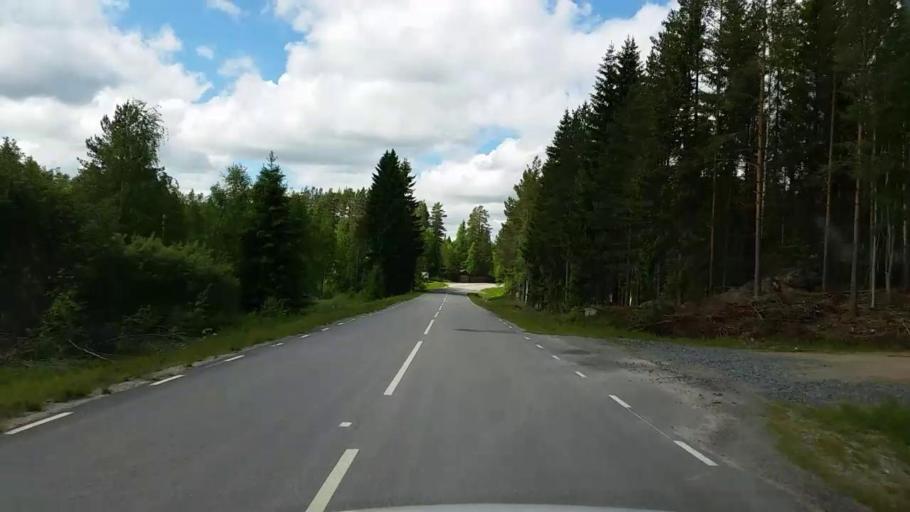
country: SE
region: Gaevleborg
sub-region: Bollnas Kommun
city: Vittsjo
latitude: 61.0633
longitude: 16.3134
